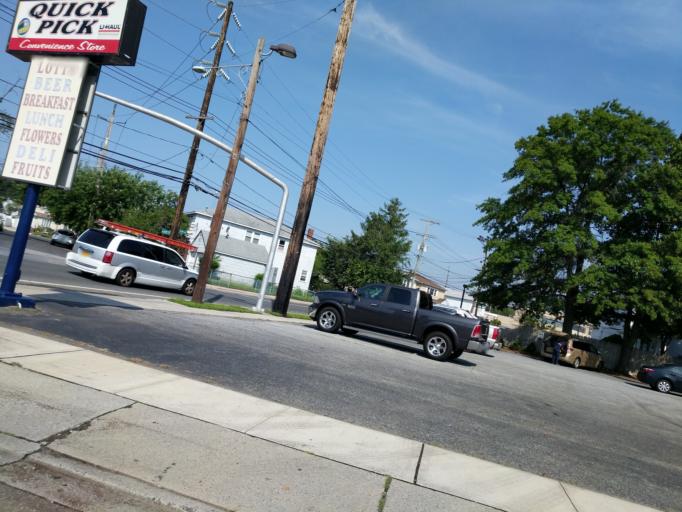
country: US
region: New York
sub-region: Nassau County
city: Valley Stream
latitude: 40.6558
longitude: -73.6999
